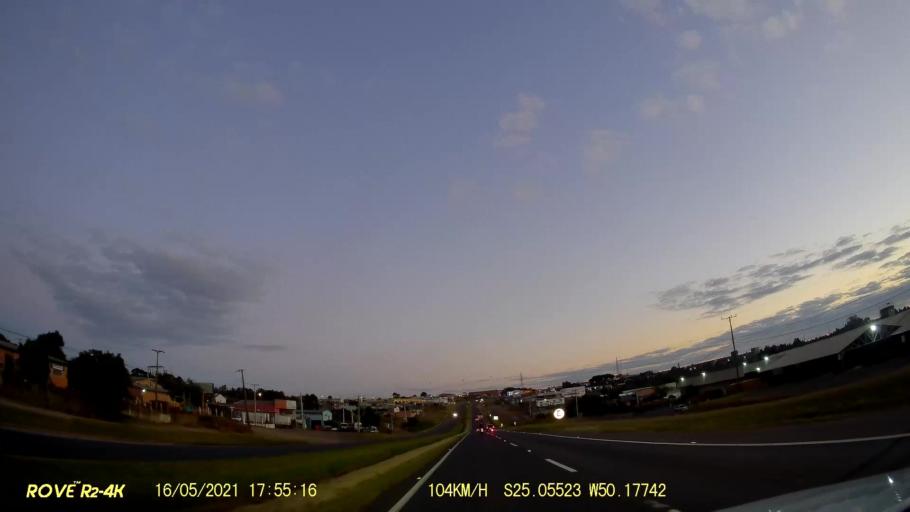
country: BR
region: Parana
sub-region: Ponta Grossa
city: Ponta Grossa
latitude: -25.0554
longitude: -50.1775
